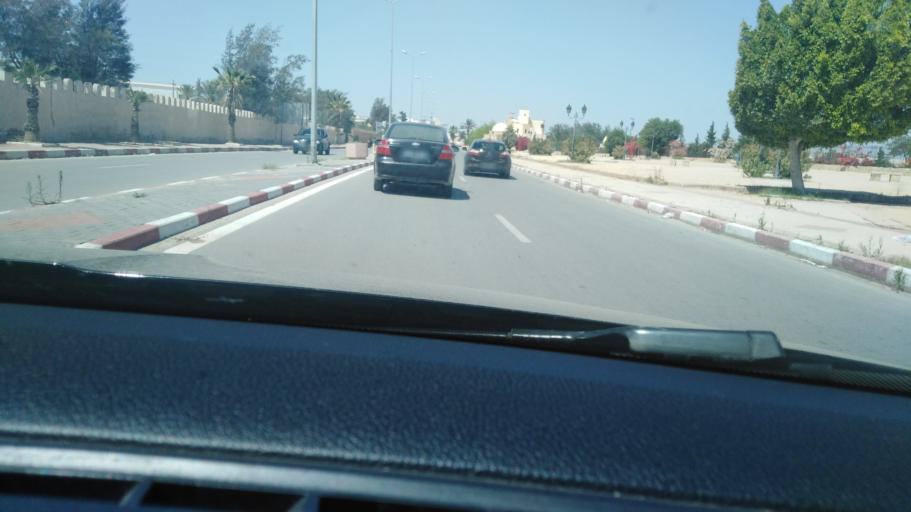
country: TN
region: Al Qayrawan
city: Kairouan
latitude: 35.6869
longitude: 10.0996
